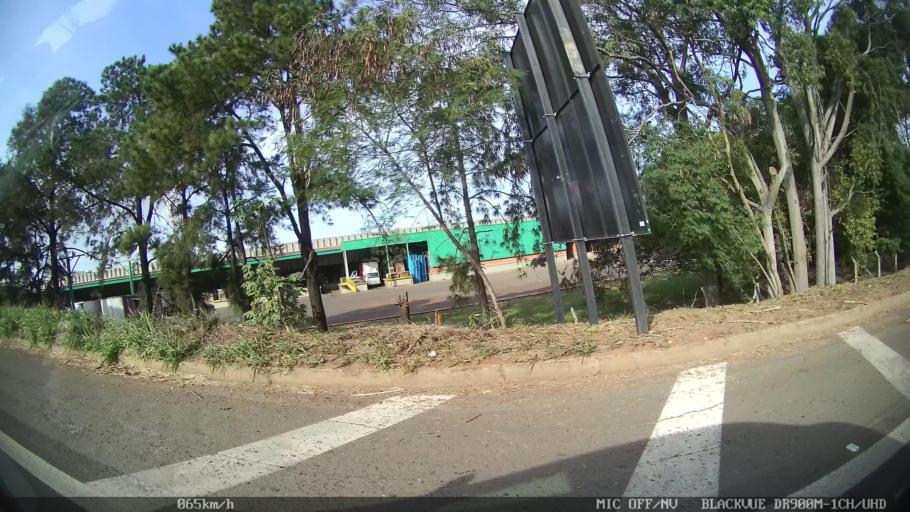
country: BR
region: Sao Paulo
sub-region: Piracicaba
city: Piracicaba
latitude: -22.6853
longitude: -47.6767
